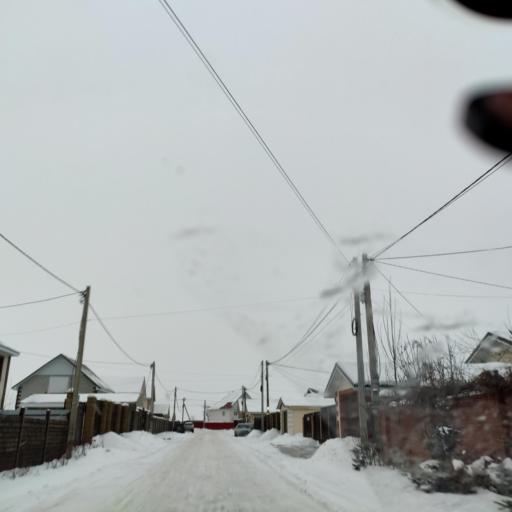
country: RU
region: Bashkortostan
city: Avdon
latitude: 54.5935
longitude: 55.8063
